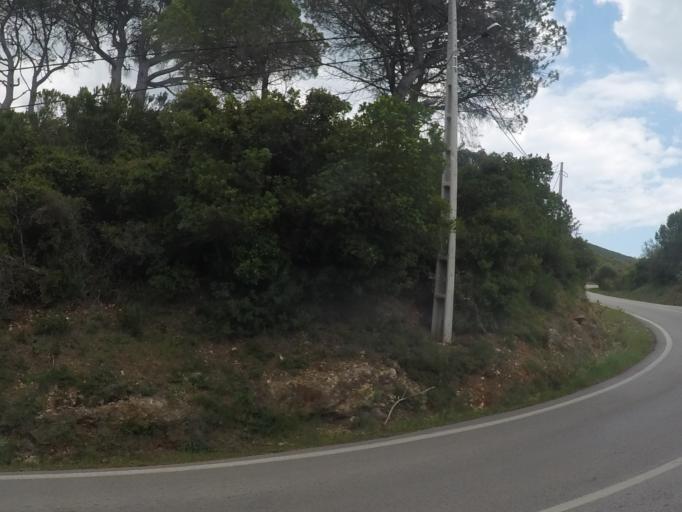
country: PT
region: Setubal
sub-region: Sesimbra
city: Sesimbra
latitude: 38.4709
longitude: -9.0305
